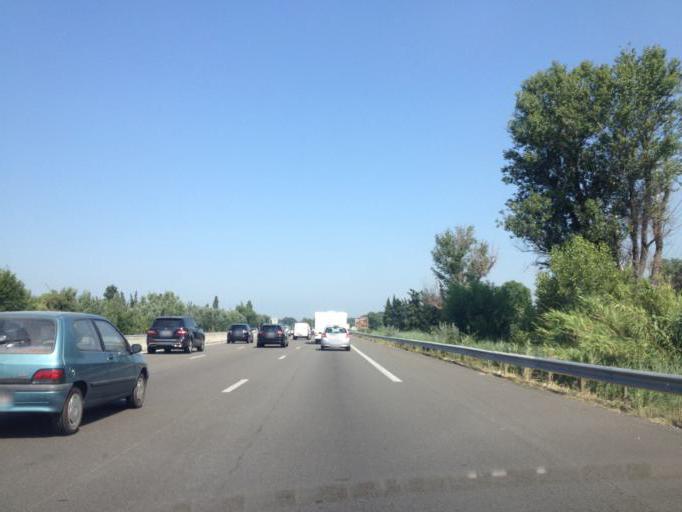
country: FR
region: Provence-Alpes-Cote d'Azur
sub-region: Departement du Vaucluse
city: Mondragon
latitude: 44.2206
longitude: 4.7171
